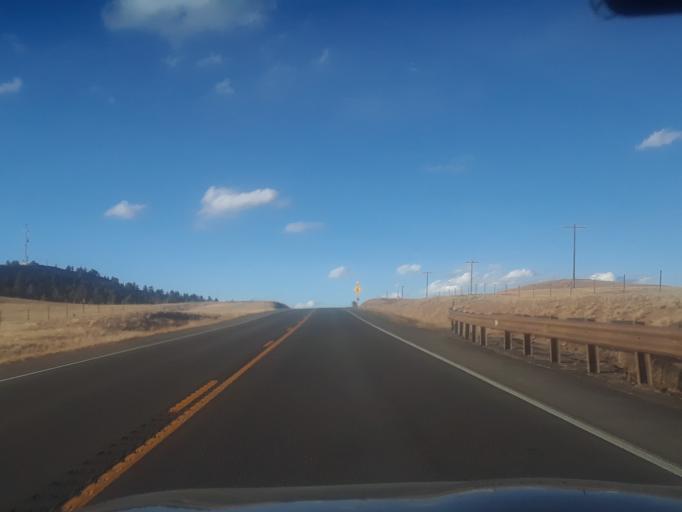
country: US
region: Colorado
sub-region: Chaffee County
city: Buena Vista
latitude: 38.9846
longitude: -105.9590
